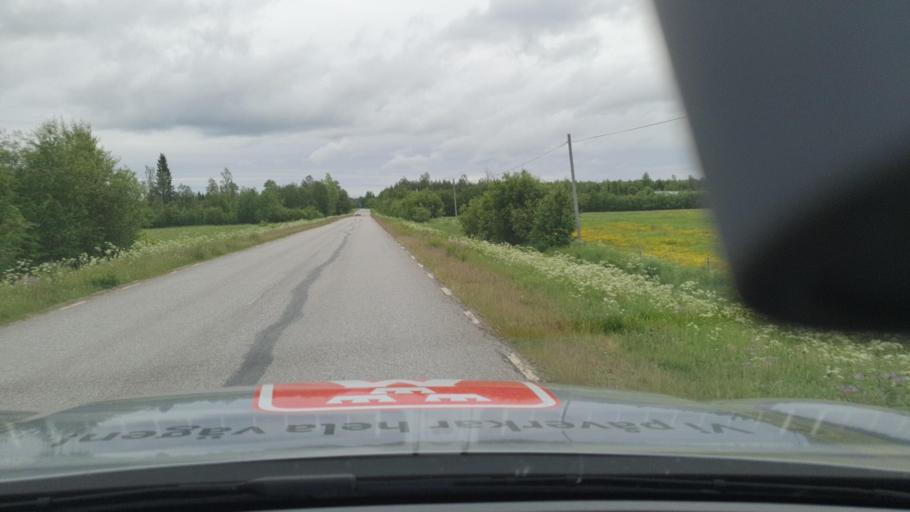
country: SE
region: Norrbotten
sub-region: Lulea Kommun
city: Ranea
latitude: 65.8466
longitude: 22.2525
